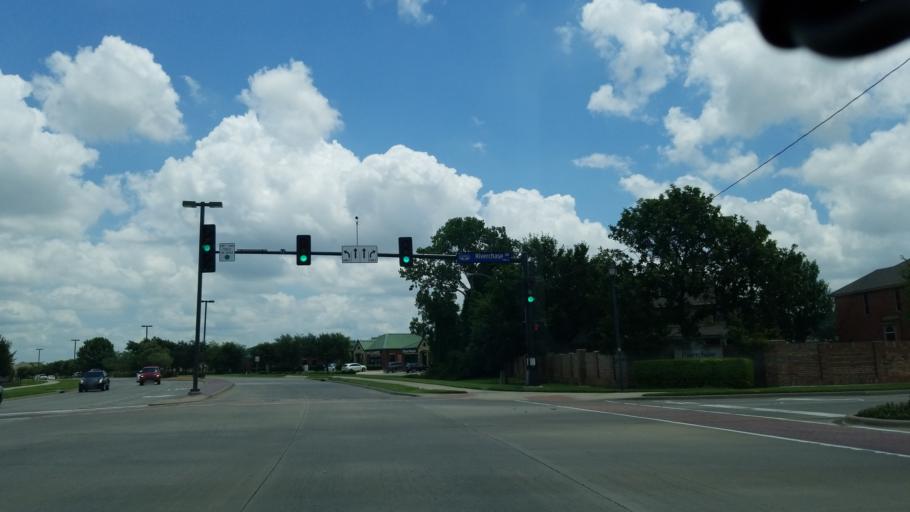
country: US
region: Texas
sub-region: Dallas County
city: Carrollton
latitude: 32.9665
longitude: -96.9514
